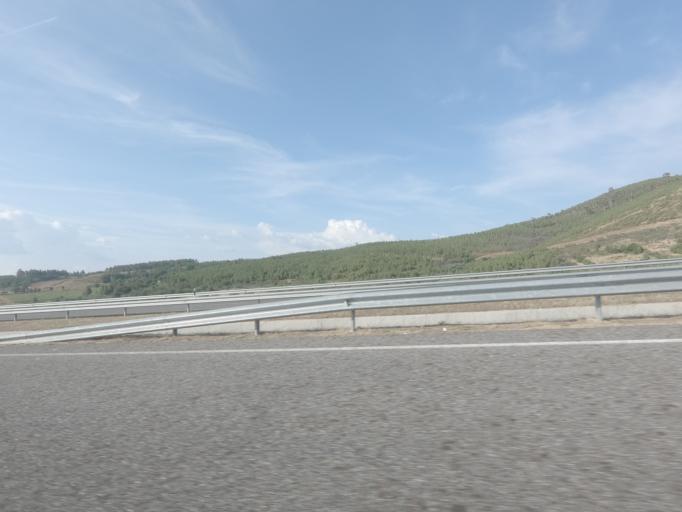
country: ES
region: Galicia
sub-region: Provincia de Ourense
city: Oimbra
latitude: 41.8653
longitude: -7.4299
